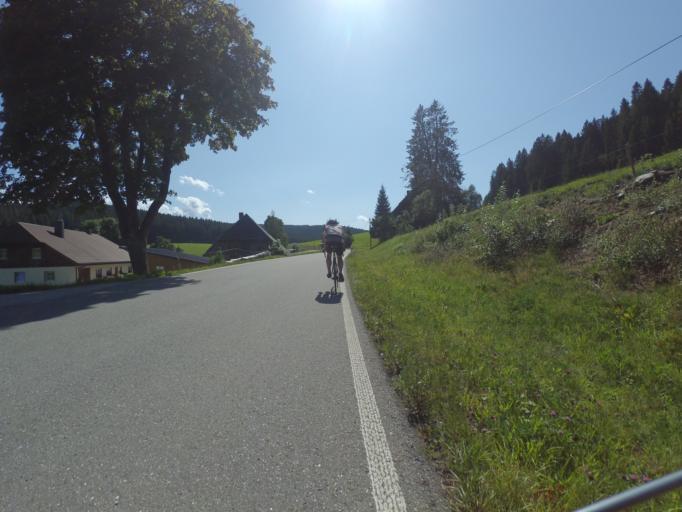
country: DE
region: Baden-Wuerttemberg
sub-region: Freiburg Region
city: Eisenbach
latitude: 47.9828
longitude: 8.2348
